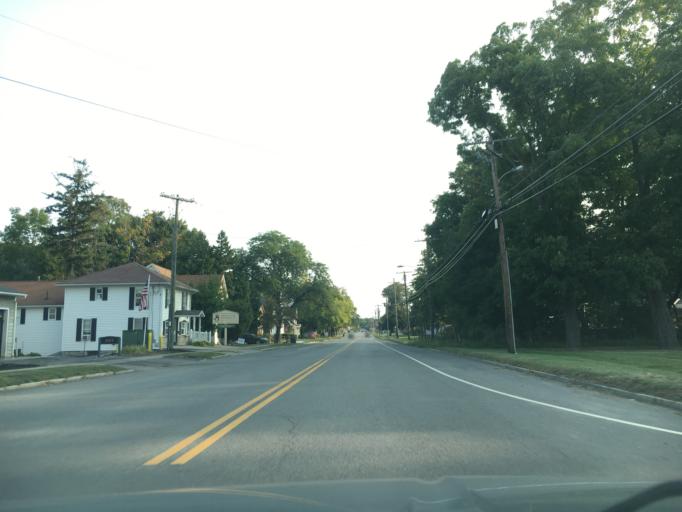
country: US
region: New York
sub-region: Yates County
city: Penn Yan
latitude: 42.6522
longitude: -77.0603
